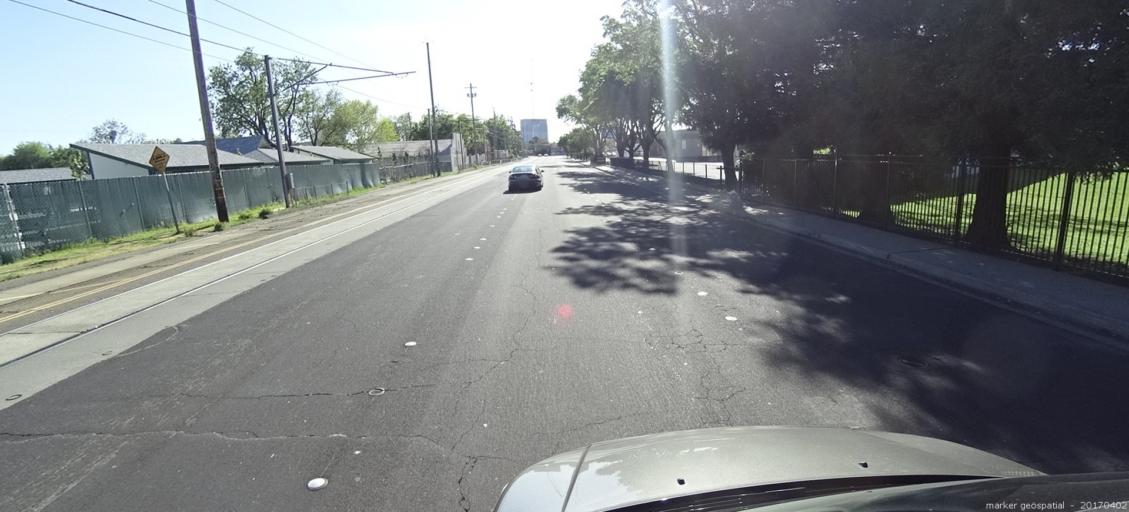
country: US
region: California
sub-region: Sacramento County
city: Sacramento
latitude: 38.5923
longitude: -121.4825
